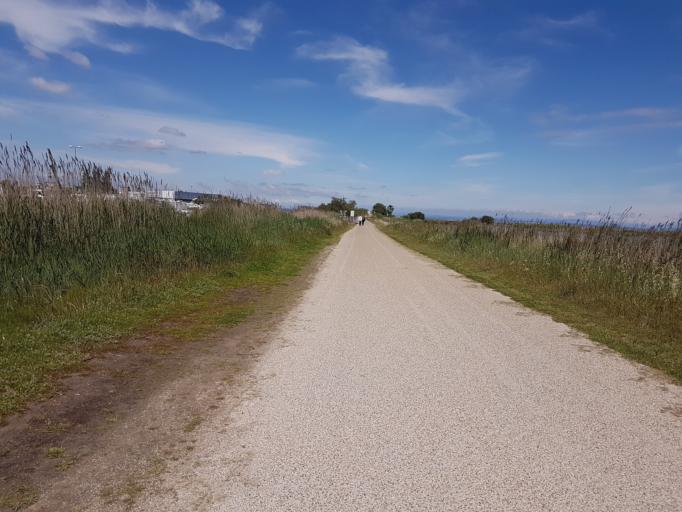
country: FR
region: Languedoc-Roussillon
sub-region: Departement de l'Herault
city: Palavas-les-Flots
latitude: 43.5324
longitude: 3.9225
